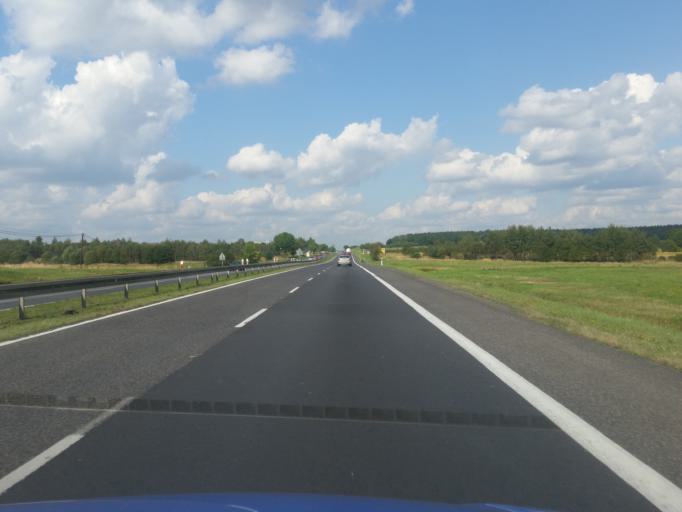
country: PL
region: Silesian Voivodeship
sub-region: Powiat myszkowski
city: Kozieglowy
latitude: 50.5494
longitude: 19.1800
